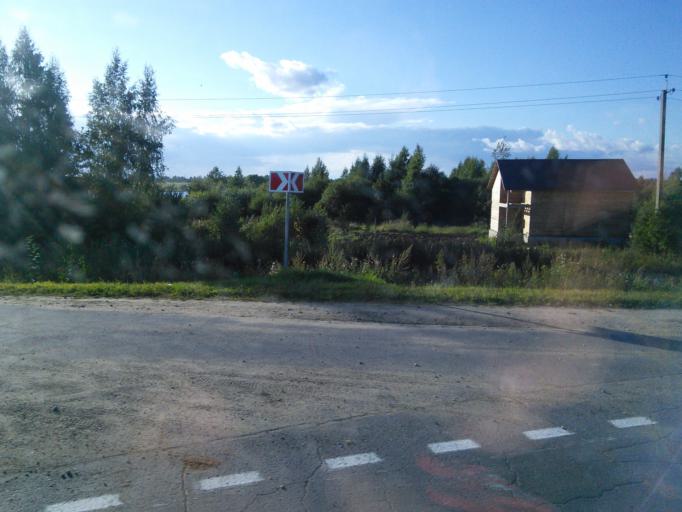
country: RU
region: Jaroslavl
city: Poshekhon'ye
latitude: 58.4925
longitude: 39.0902
